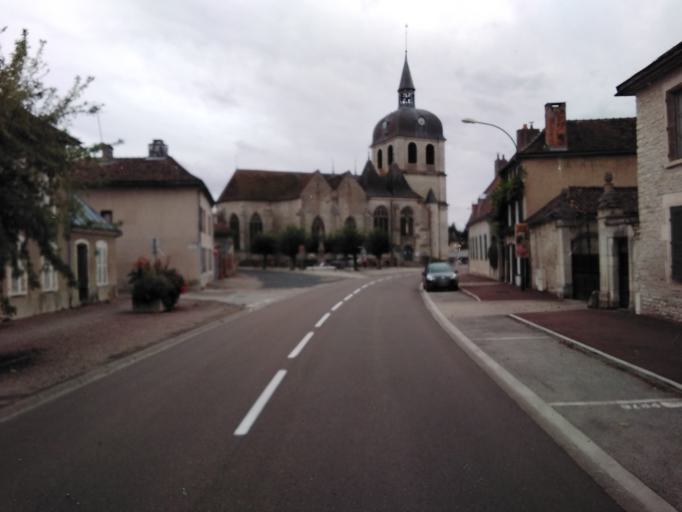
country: FR
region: Champagne-Ardenne
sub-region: Departement de l'Aube
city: Brienne-le-Chateau
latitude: 48.3500
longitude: 4.5323
